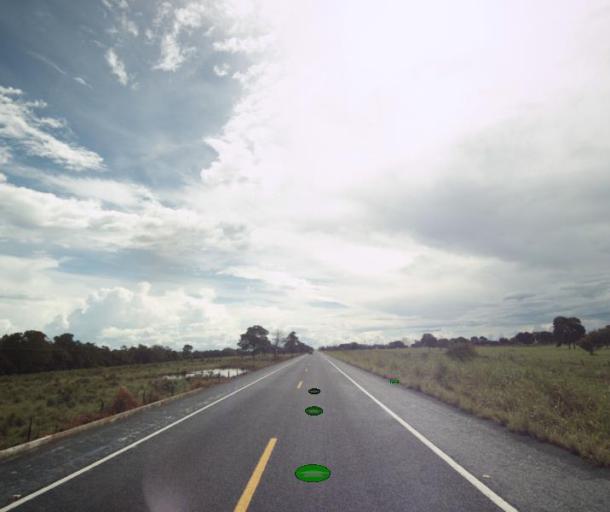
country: BR
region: Goias
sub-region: Sao Miguel Do Araguaia
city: Sao Miguel do Araguaia
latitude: -13.2916
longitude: -50.4102
